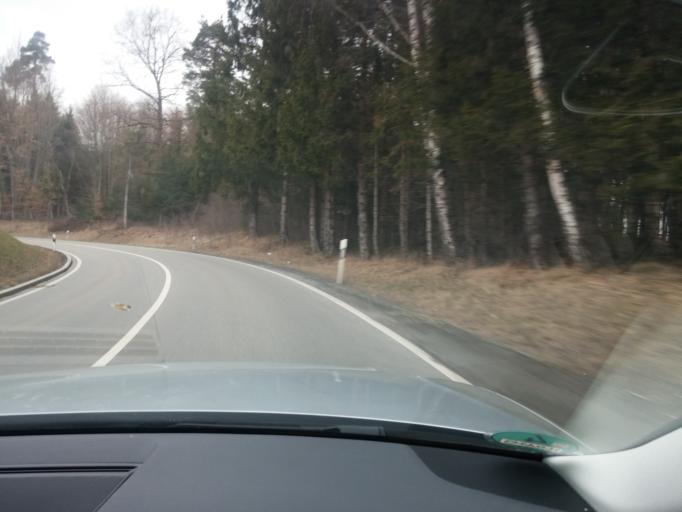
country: DE
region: Bavaria
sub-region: Upper Bavaria
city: Glonn
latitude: 47.9972
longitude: 11.8548
